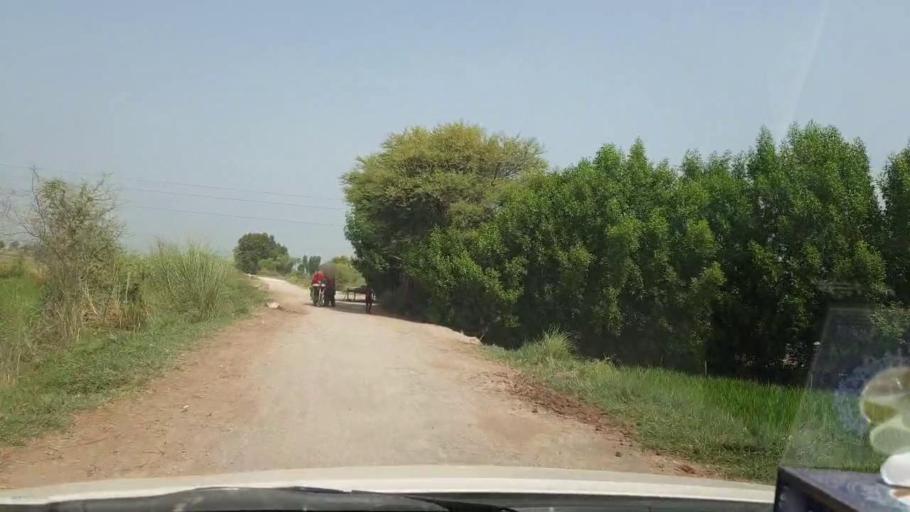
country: PK
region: Sindh
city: Shikarpur
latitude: 27.9882
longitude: 68.6979
